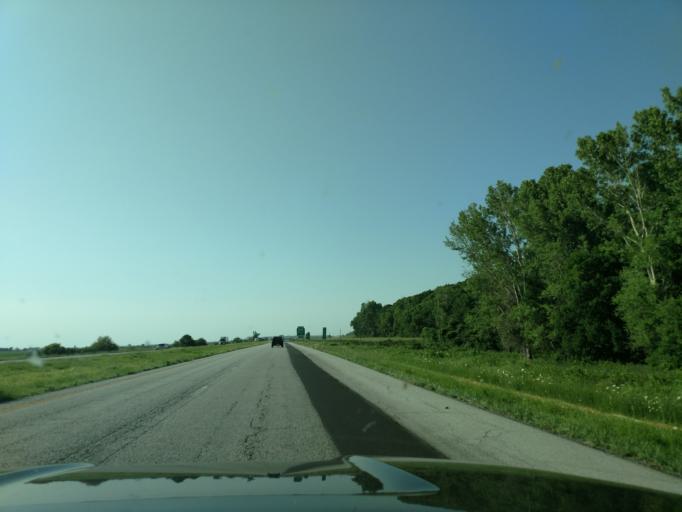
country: US
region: Missouri
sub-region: Atchison County
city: Rock Port
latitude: 40.4572
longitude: -95.5846
